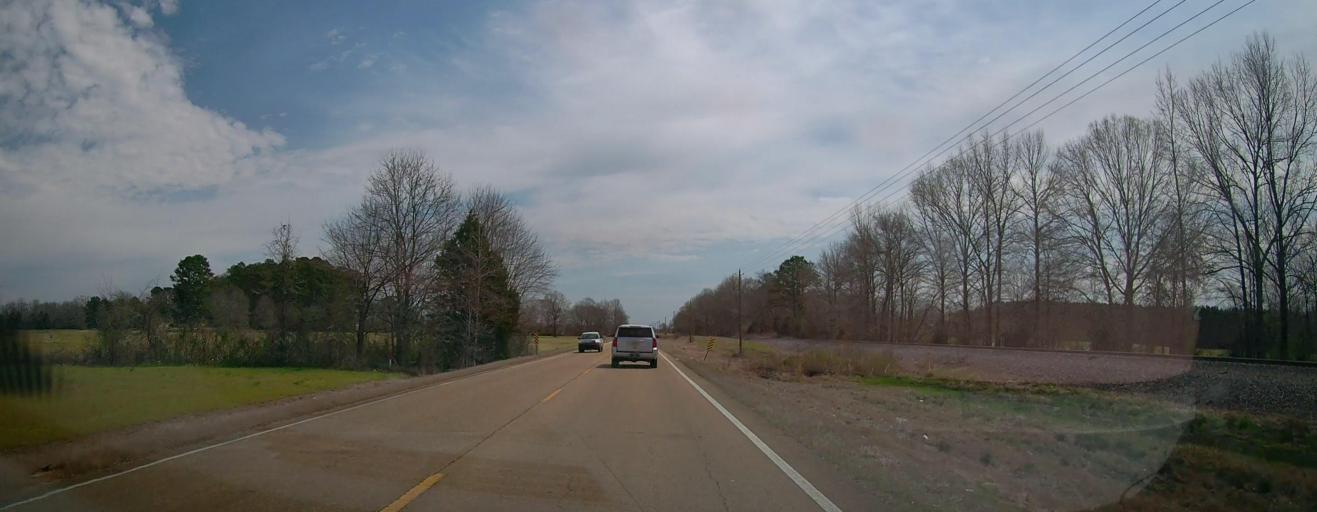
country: US
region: Mississippi
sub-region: Benton County
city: Ashland
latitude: 34.6251
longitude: -89.2516
